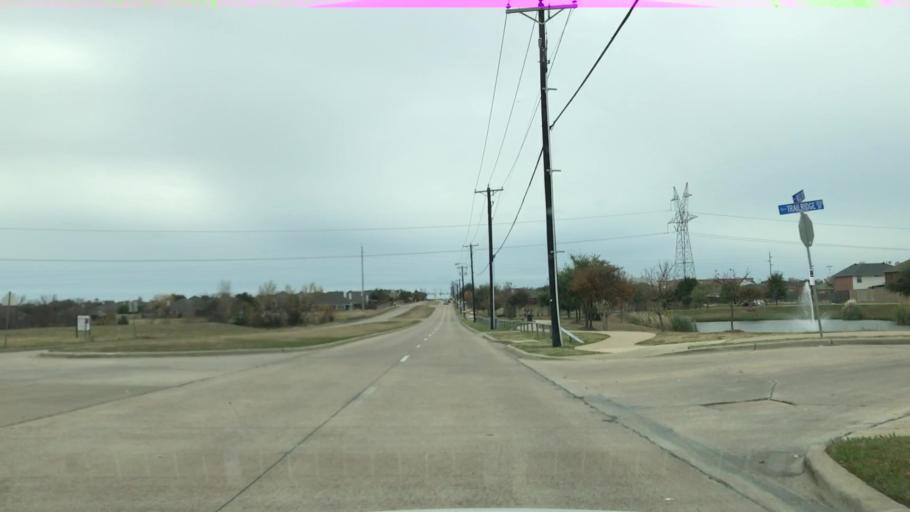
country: US
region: Texas
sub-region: Dallas County
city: Sachse
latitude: 32.9686
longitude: -96.5835
